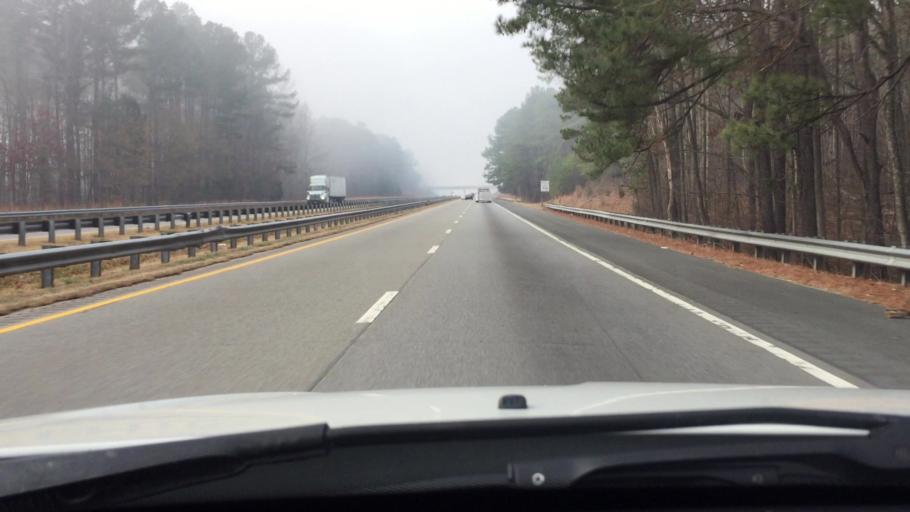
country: US
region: North Carolina
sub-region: Wake County
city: Holly Springs
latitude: 35.6650
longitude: -78.9388
